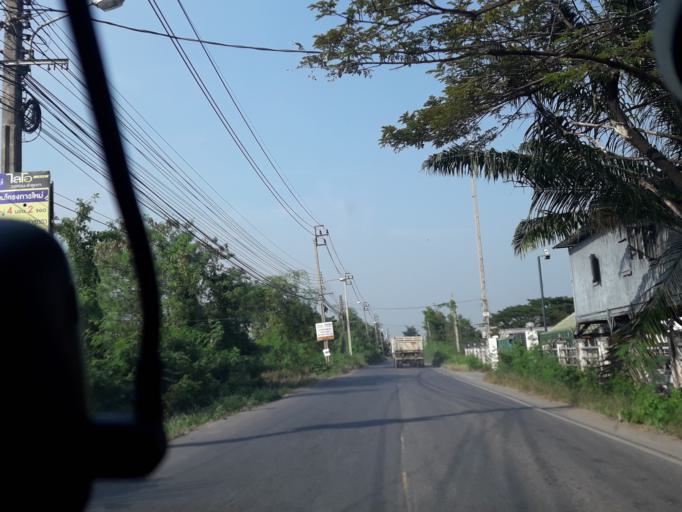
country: TH
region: Pathum Thani
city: Lam Luk Ka
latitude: 13.9080
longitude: 100.7363
